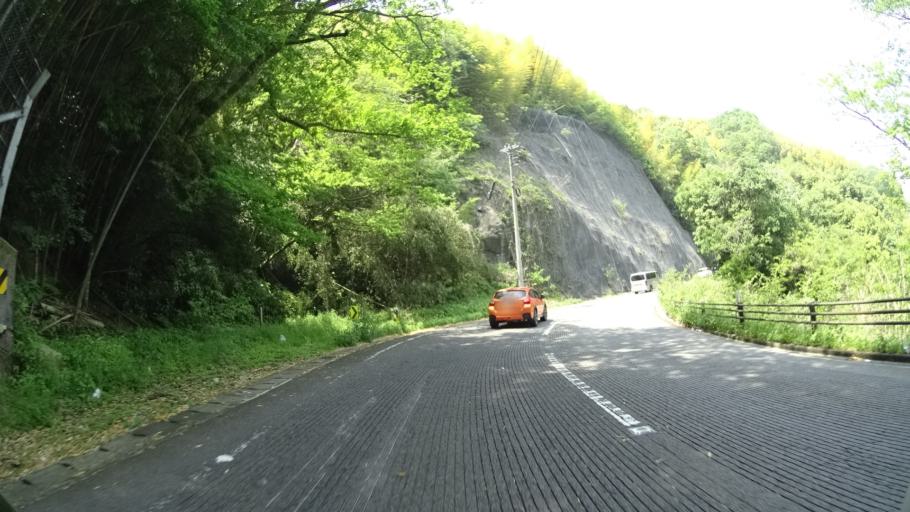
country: JP
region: Ehime
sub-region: Shikoku-chuo Shi
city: Matsuyama
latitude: 33.8778
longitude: 132.8358
